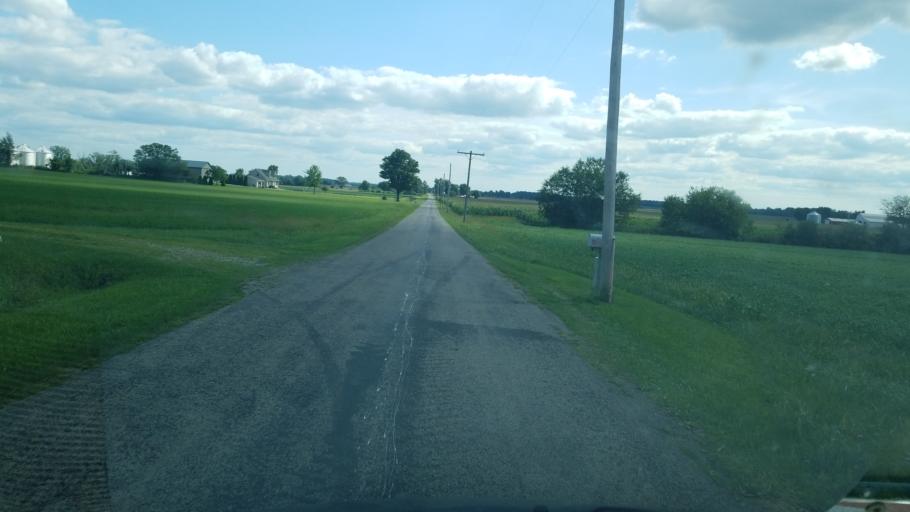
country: US
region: Ohio
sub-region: Logan County
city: Lakeview
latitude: 40.5344
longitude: -83.9749
